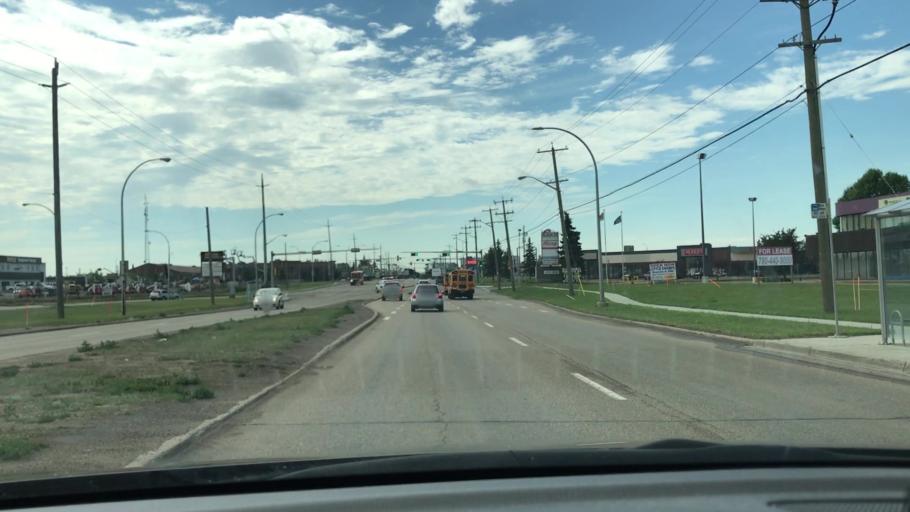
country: CA
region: Alberta
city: Edmonton
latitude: 53.5173
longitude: -113.4186
